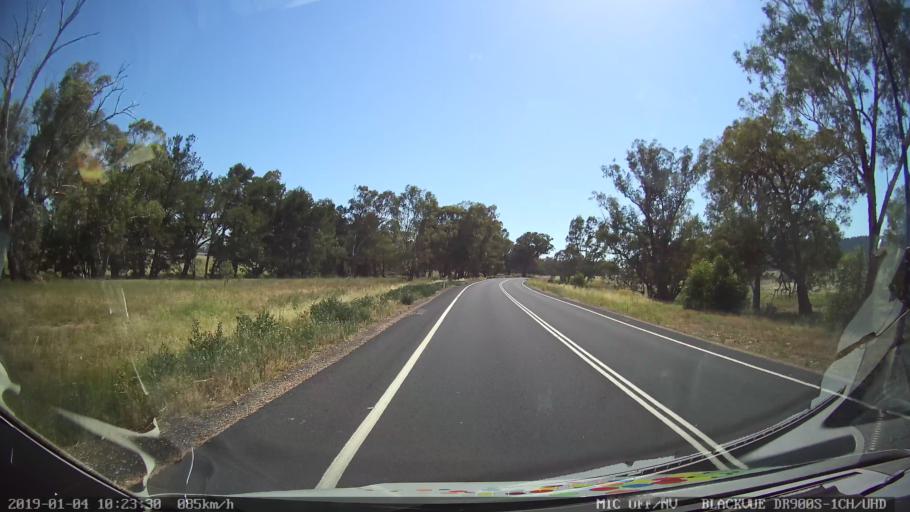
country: AU
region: New South Wales
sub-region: Cabonne
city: Canowindra
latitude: -33.3710
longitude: 148.5404
